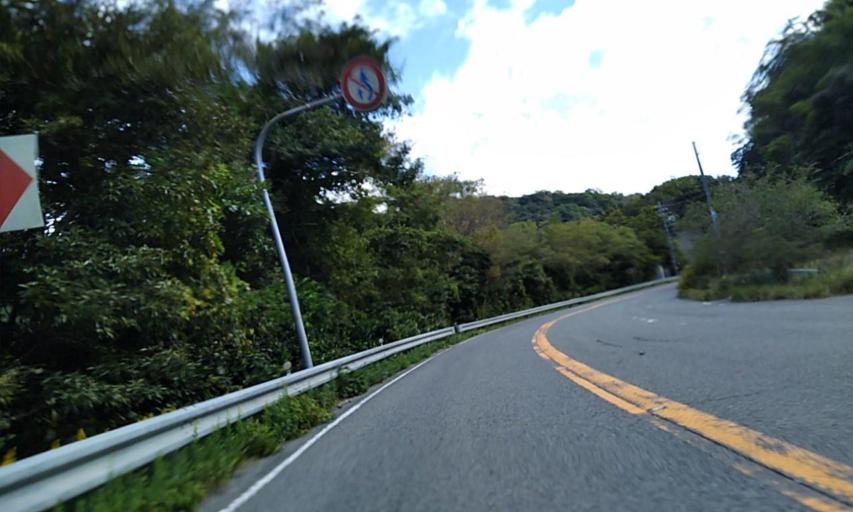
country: JP
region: Wakayama
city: Gobo
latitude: 33.9413
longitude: 135.1332
